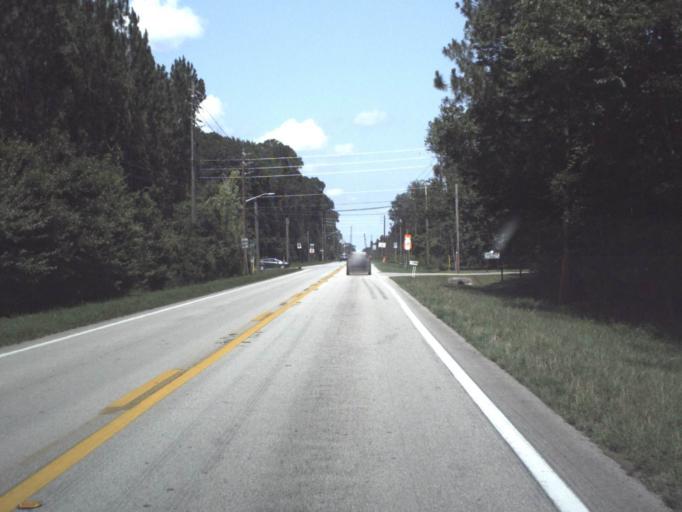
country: US
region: Florida
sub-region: Duval County
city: Baldwin
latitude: 30.3093
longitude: -81.8959
